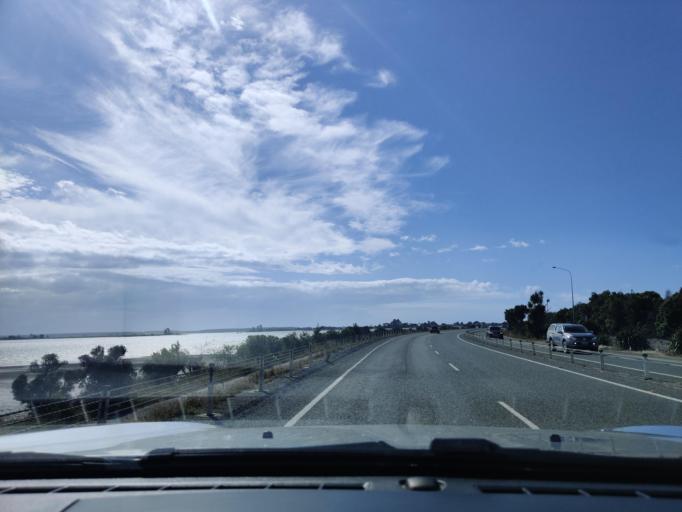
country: NZ
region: Tasman
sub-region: Tasman District
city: Richmond
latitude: -41.3207
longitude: 173.2108
